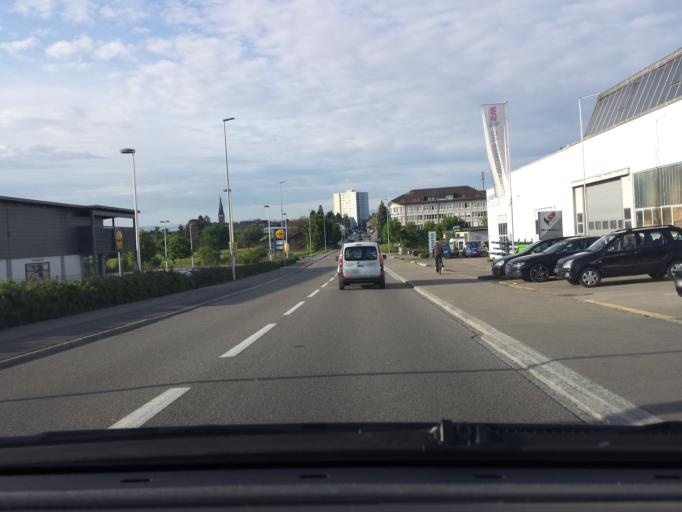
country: CH
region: Thurgau
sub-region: Arbon District
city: Romanshorn
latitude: 47.5720
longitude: 9.3658
